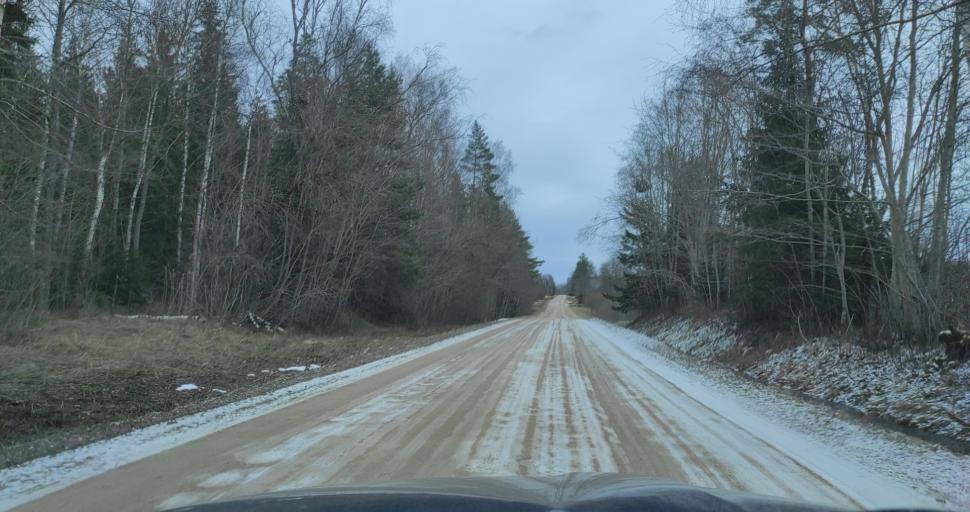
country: LV
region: Tukuma Rajons
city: Tukums
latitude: 57.0815
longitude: 23.0748
